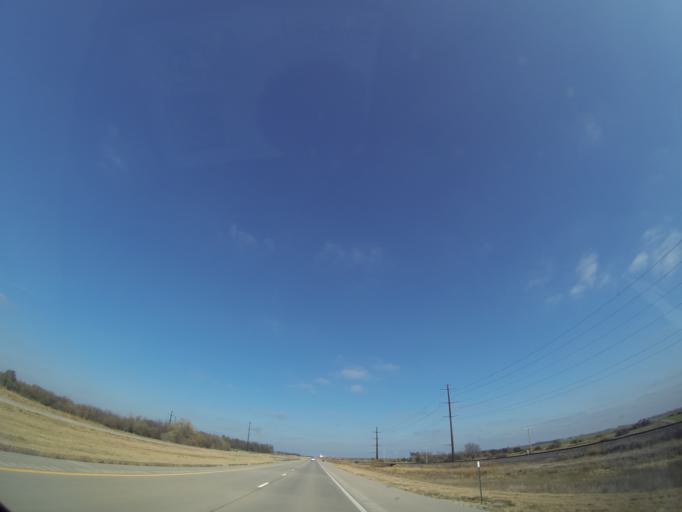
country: US
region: Kansas
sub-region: McPherson County
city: Inman
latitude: 38.1983
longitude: -97.8037
